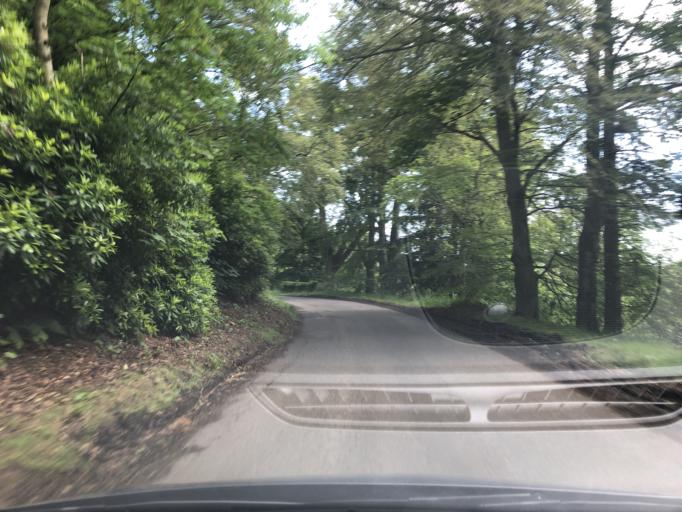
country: GB
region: Scotland
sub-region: Angus
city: Kirriemuir
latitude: 56.7254
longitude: -2.9822
